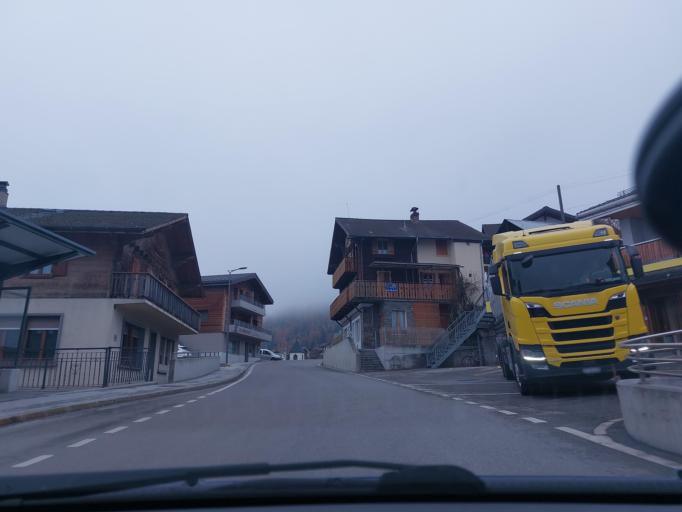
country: CH
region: Valais
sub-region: Conthey District
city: Basse-Nendaz
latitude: 46.1869
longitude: 7.2976
